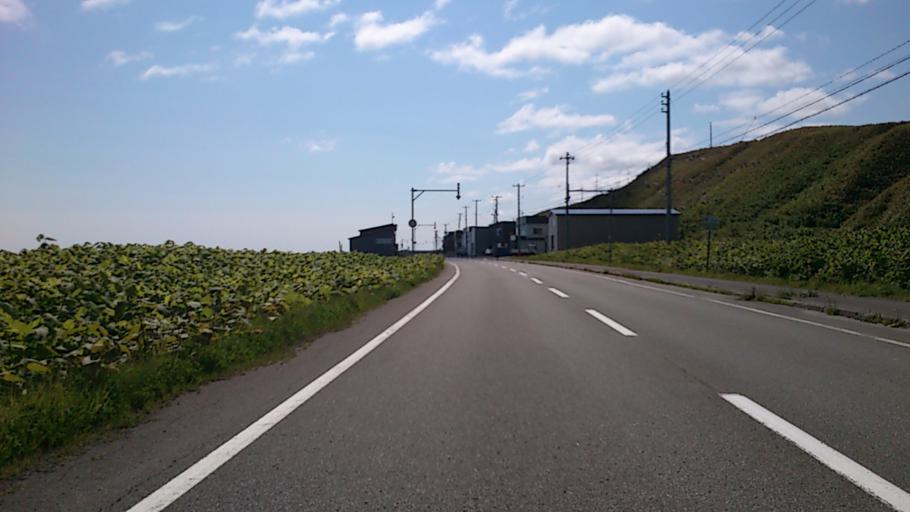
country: JP
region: Hokkaido
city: Makubetsu
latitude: 45.3852
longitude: 142.0791
